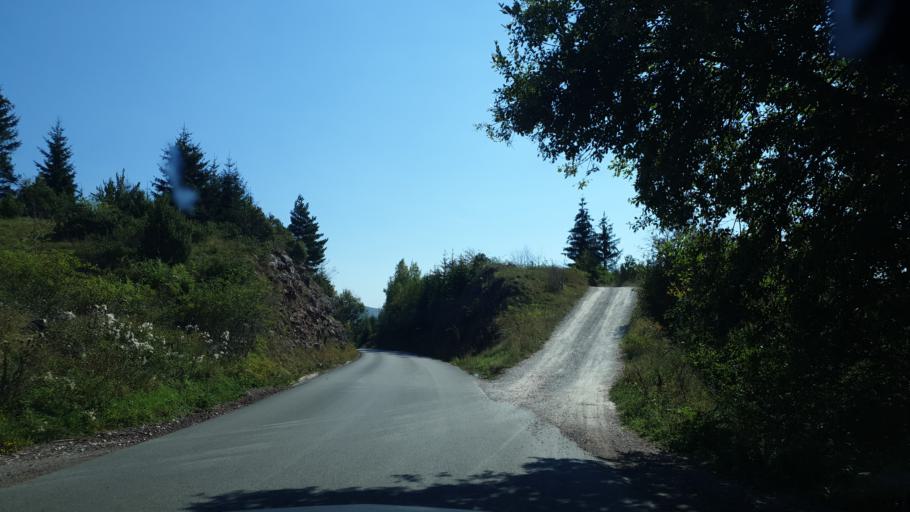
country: RS
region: Central Serbia
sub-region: Zlatiborski Okrug
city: Nova Varos
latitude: 43.4262
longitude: 19.8999
